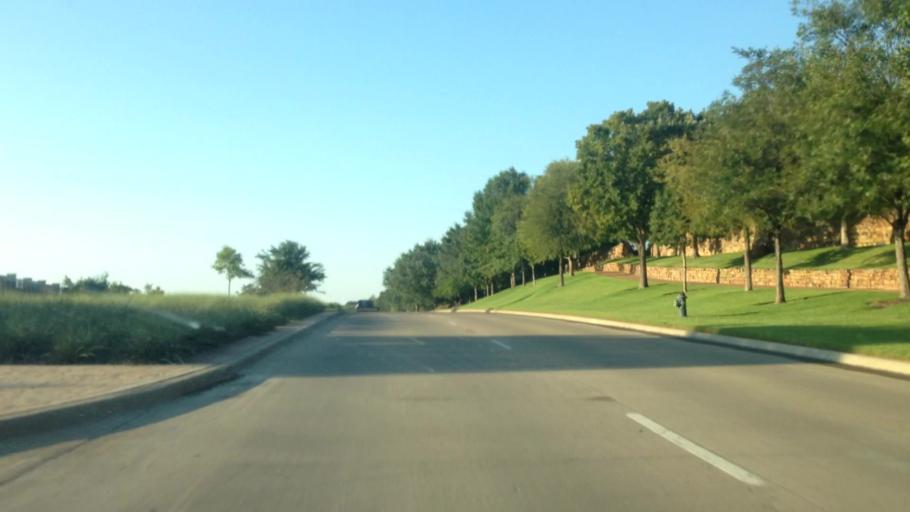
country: US
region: Texas
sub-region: Denton County
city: Trophy Club
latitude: 32.9741
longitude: -97.1864
